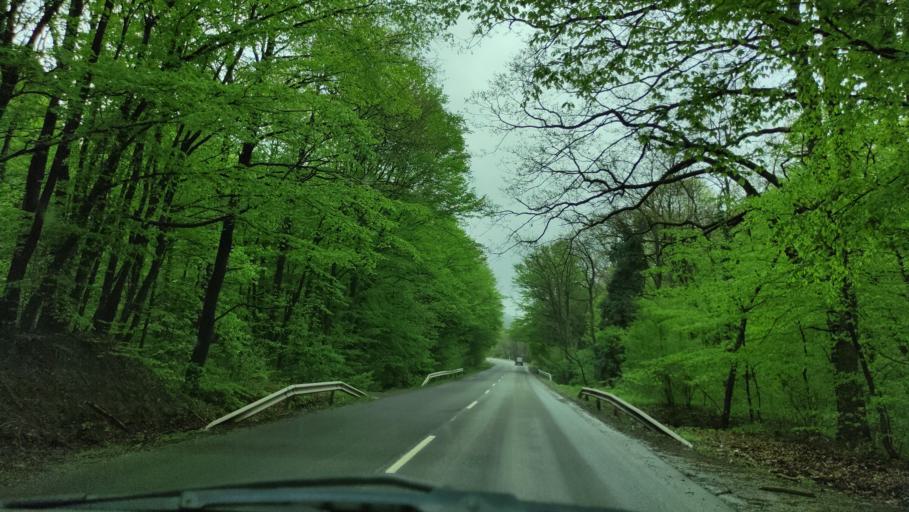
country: HU
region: Baranya
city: Komlo
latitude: 46.1852
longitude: 18.3074
